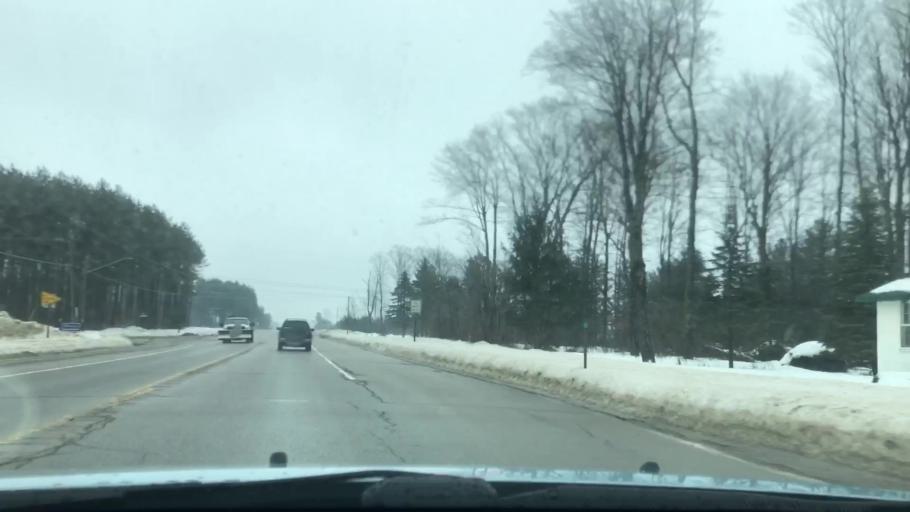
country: US
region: Michigan
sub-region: Otsego County
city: Gaylord
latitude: 45.0276
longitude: -84.7363
